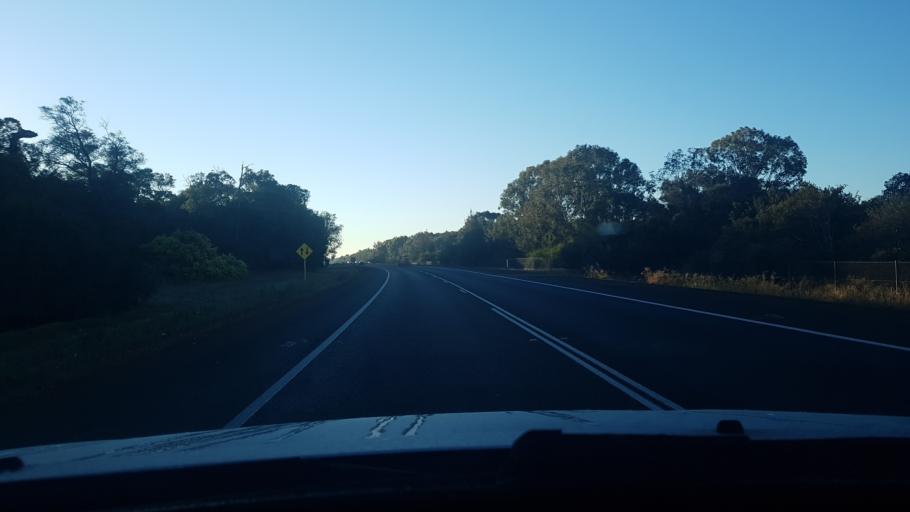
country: AU
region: Western Australia
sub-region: Busselton
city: Vasse
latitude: -33.6763
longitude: 115.2678
